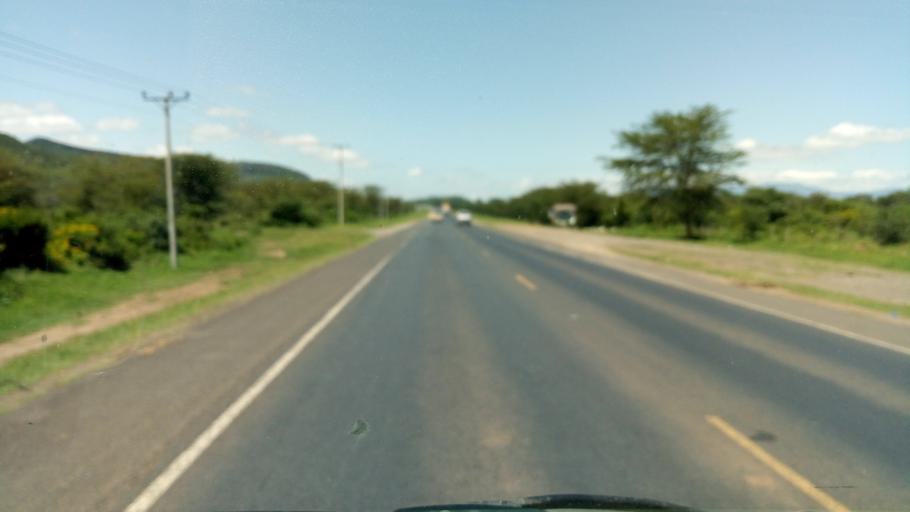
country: KE
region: Nyandarua
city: Ol Kalou
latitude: -0.4050
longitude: 36.2513
